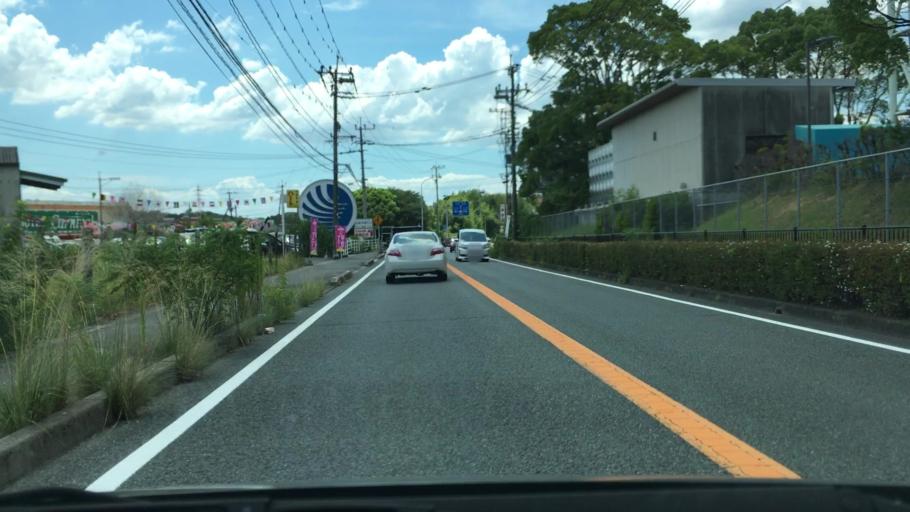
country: JP
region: Saga Prefecture
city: Kanzakimachi-kanzaki
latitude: 33.3386
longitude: 130.4301
